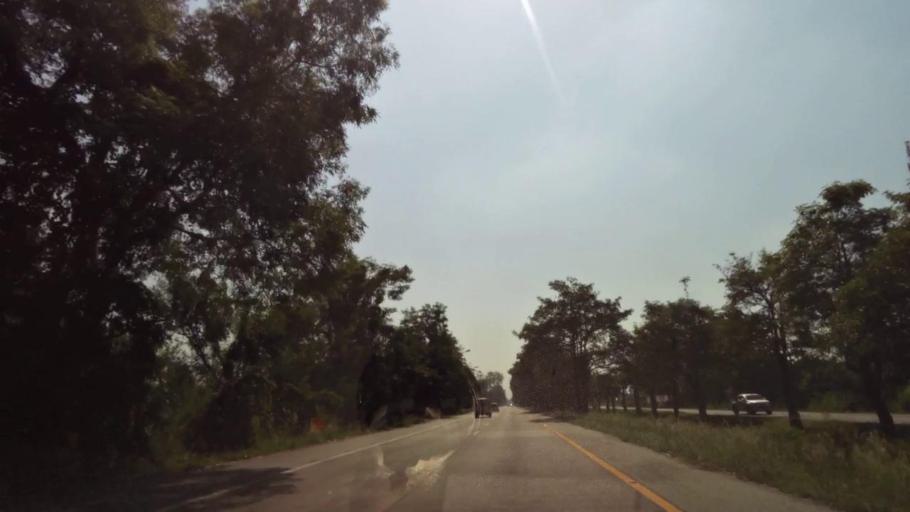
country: TH
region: Phichit
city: Wachira Barami
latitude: 16.6368
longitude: 100.1496
